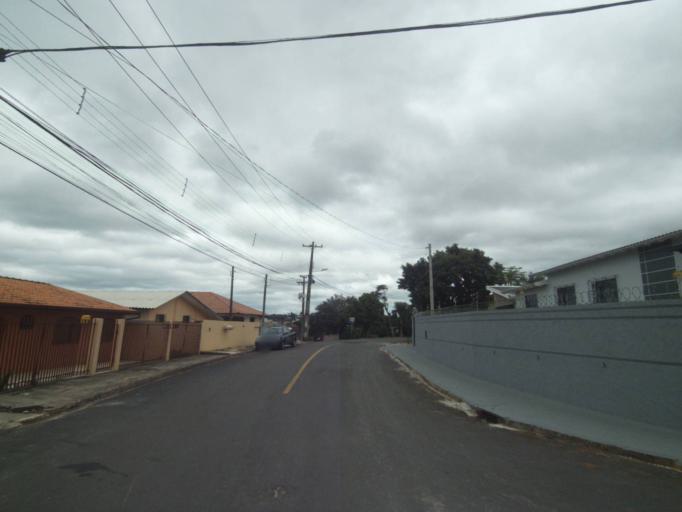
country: BR
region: Parana
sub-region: Telemaco Borba
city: Telemaco Borba
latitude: -24.3342
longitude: -50.6082
